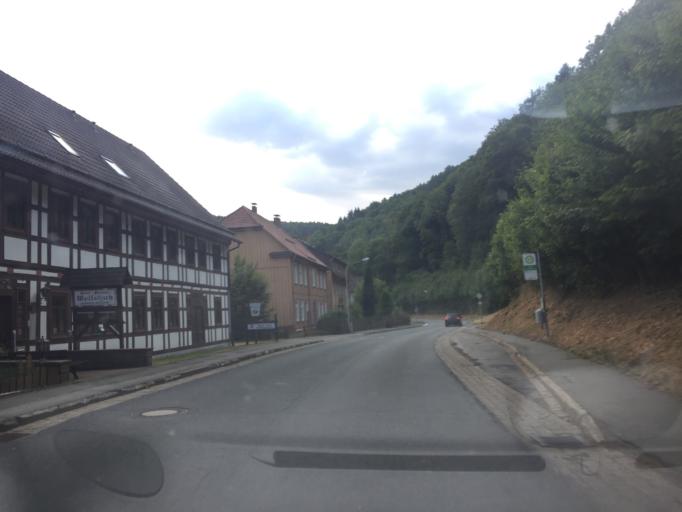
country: DE
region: Lower Saxony
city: Zorge
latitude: 51.6402
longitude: 10.6382
